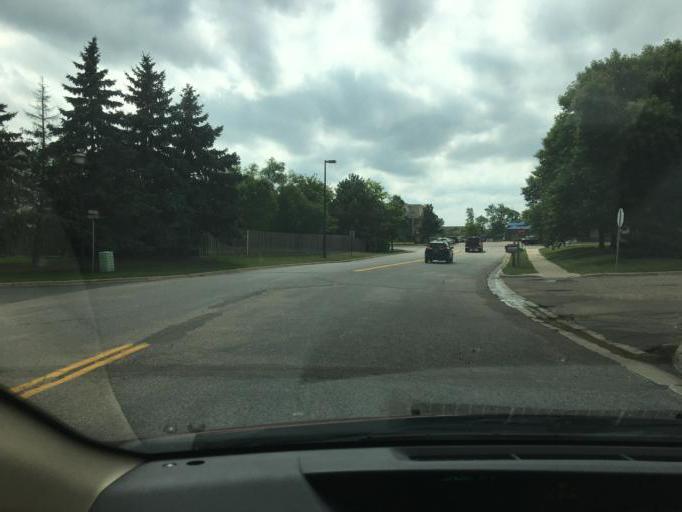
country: US
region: Minnesota
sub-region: Carver County
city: Chanhassen
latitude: 44.8577
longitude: -93.5298
